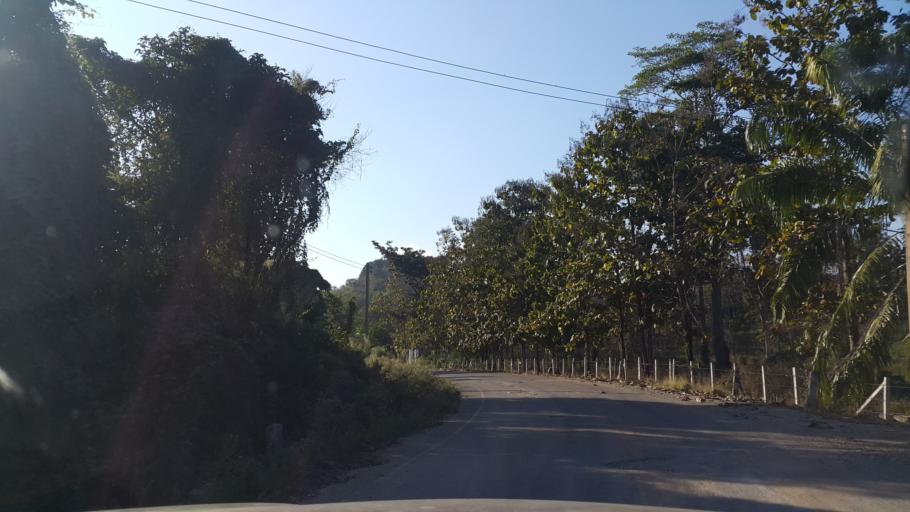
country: TH
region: Sukhothai
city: Thung Saliam
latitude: 17.3885
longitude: 99.5121
